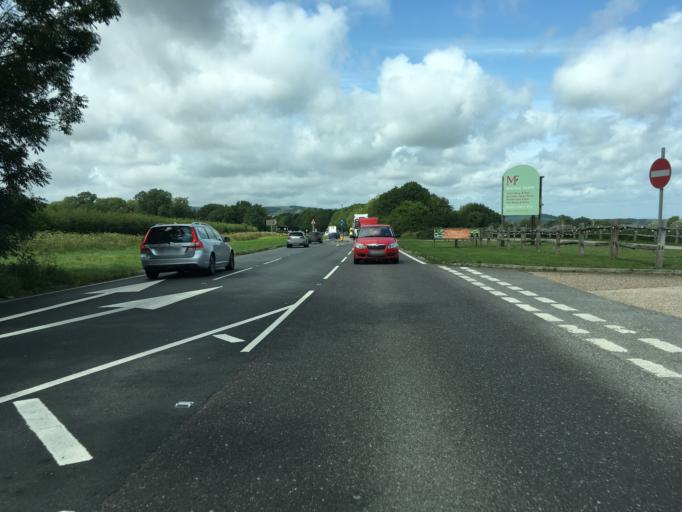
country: GB
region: England
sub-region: East Sussex
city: Ringmer
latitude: 50.8512
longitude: 0.1115
